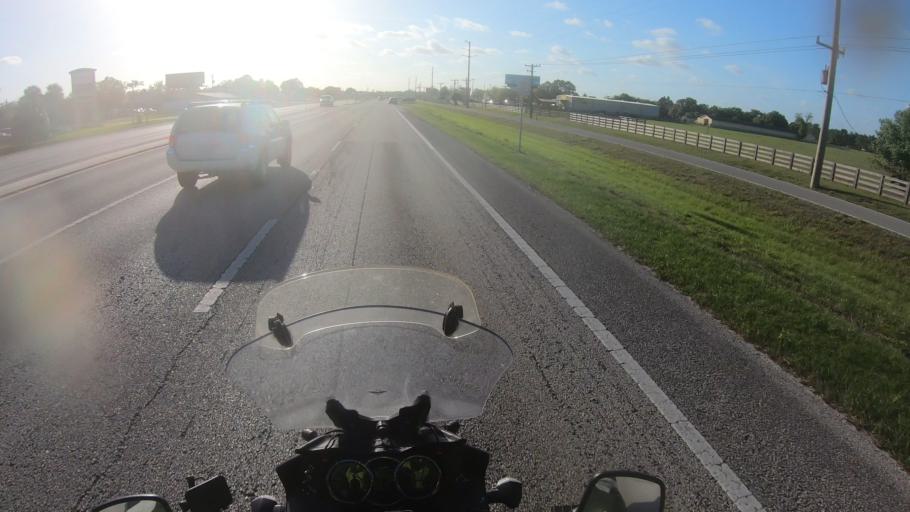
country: US
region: Florida
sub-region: DeSoto County
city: Arcadia
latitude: 27.2098
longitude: -81.8359
